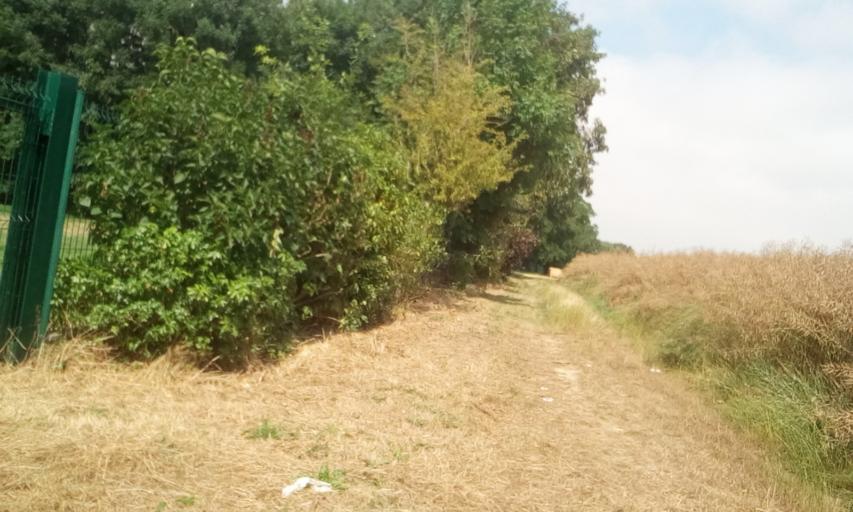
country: FR
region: Lower Normandy
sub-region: Departement du Calvados
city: Douvres-la-Delivrande
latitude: 49.2956
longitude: -0.4105
